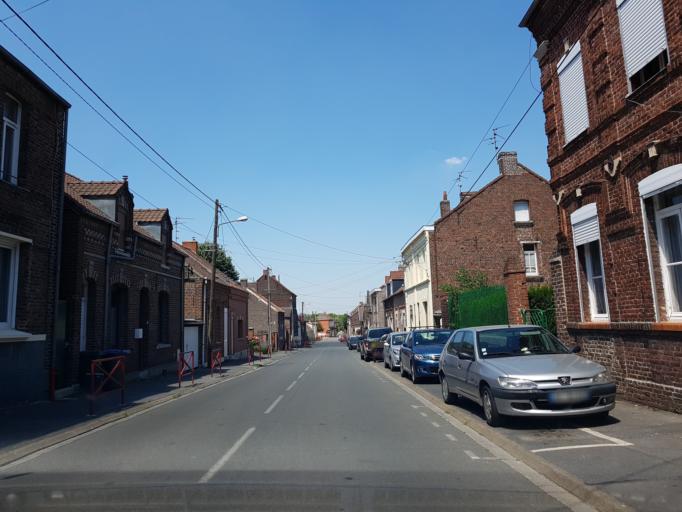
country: FR
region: Nord-Pas-de-Calais
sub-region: Departement du Nord
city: Neuville-sur-Escaut
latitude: 50.2988
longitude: 3.3555
